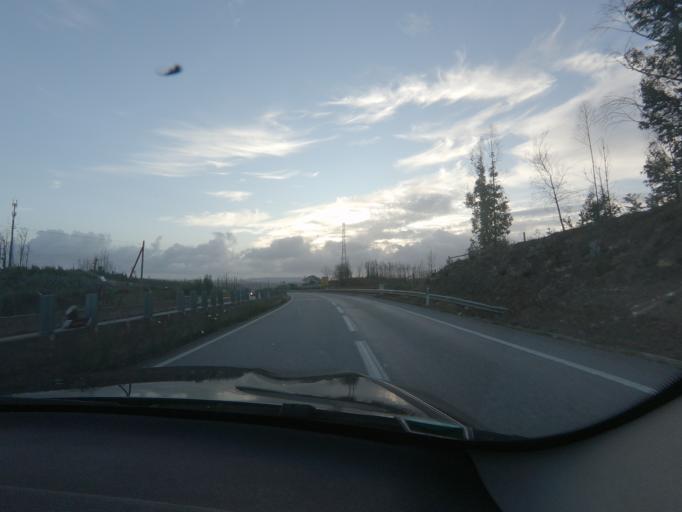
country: PT
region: Viseu
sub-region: Mortagua
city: Mortagua
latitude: 40.3538
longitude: -8.1979
